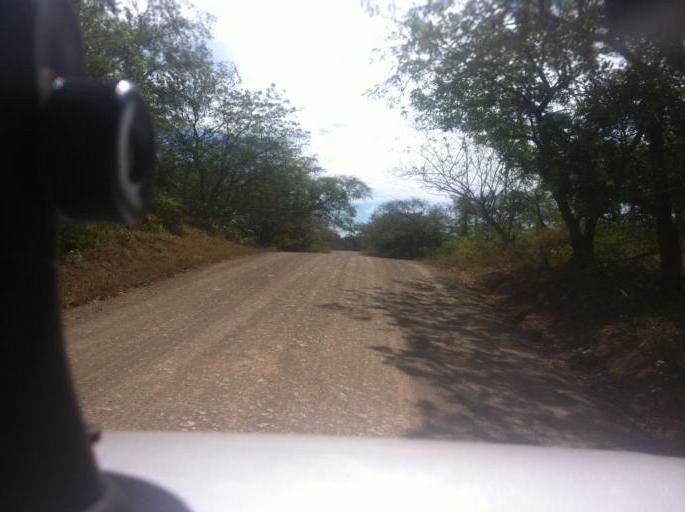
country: NI
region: Rivas
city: Tola
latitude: 11.5582
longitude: -86.0323
